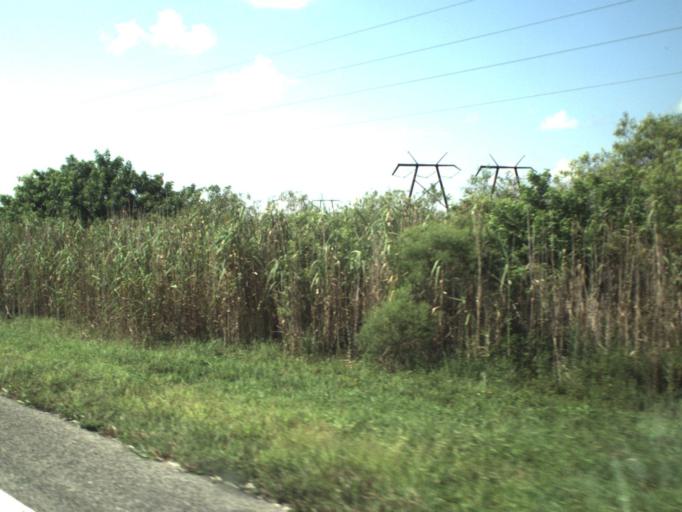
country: US
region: Florida
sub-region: Broward County
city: Weston
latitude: 26.3119
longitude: -80.5203
